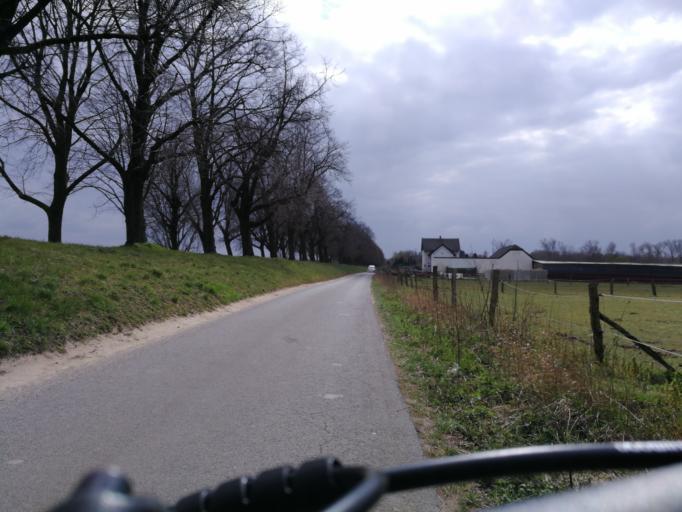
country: DE
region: North Rhine-Westphalia
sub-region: Regierungsbezirk Dusseldorf
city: Neuss
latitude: 51.1981
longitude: 6.7255
